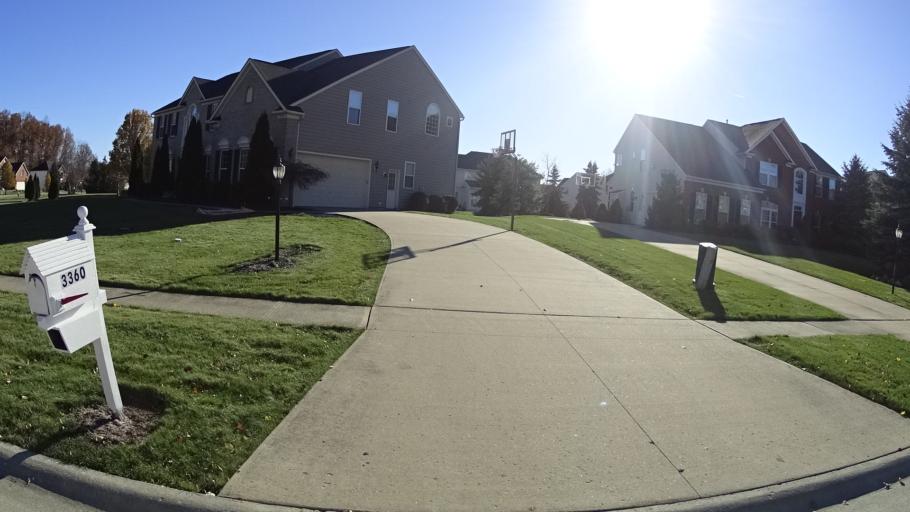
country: US
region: Ohio
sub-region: Lorain County
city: Avon Center
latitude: 41.4414
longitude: -81.9836
